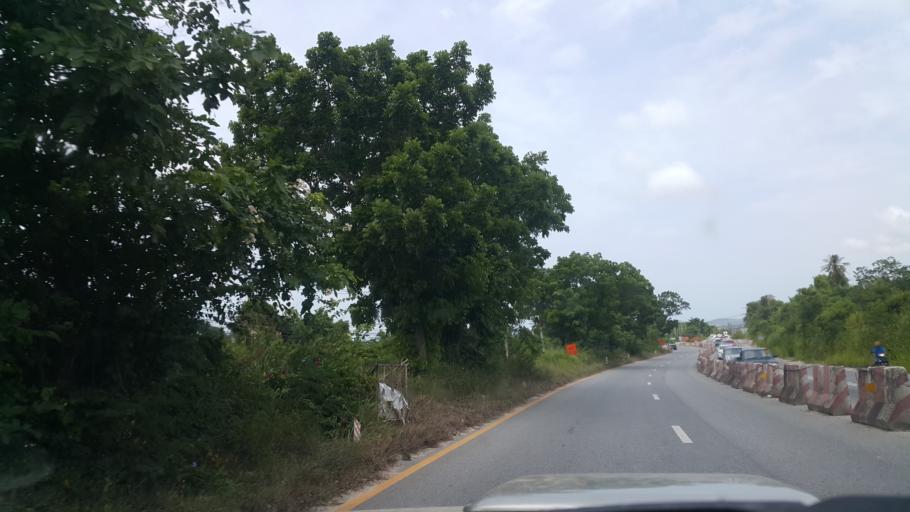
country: TH
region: Rayong
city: Ban Chang
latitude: 12.7094
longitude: 101.0260
